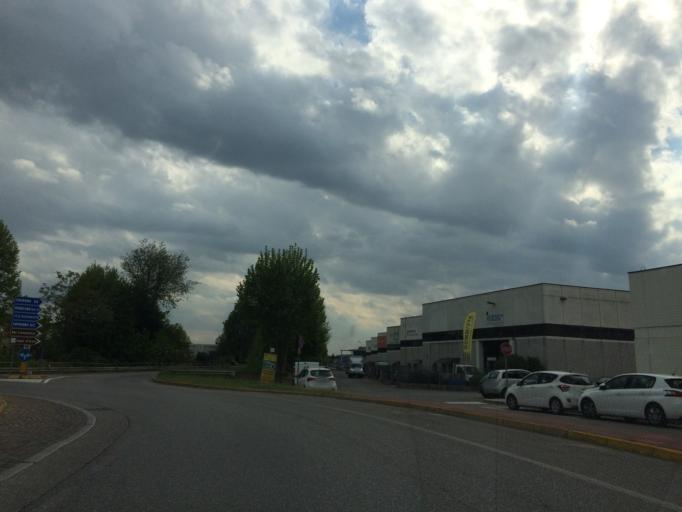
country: IT
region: Lombardy
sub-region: Provincia di Brescia
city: Castel Mella
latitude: 45.4862
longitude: 10.1493
